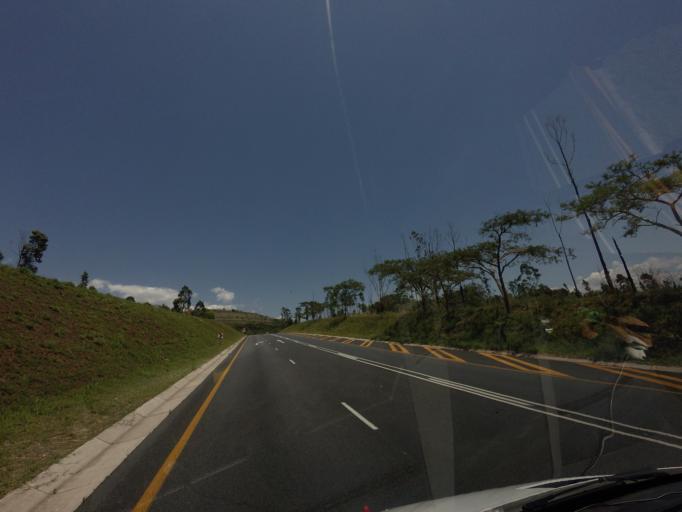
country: ZA
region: Mpumalanga
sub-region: Ehlanzeni District
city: Nelspruit
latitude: -25.4562
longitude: 30.6837
